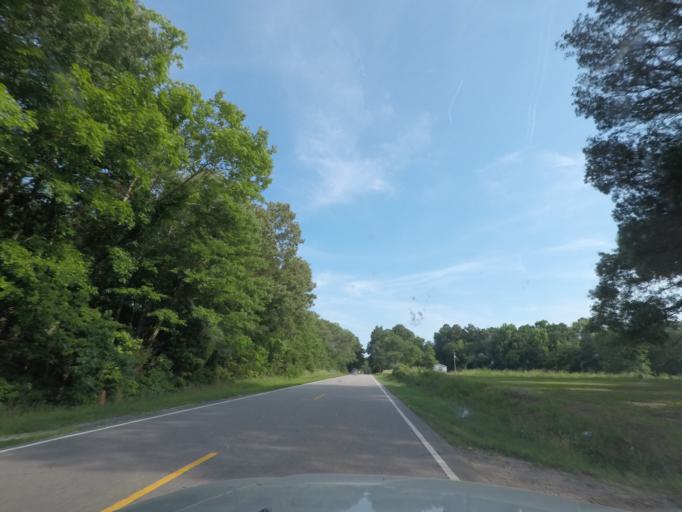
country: US
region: Virginia
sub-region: Mecklenburg County
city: Clarksville
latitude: 36.5244
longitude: -78.5349
